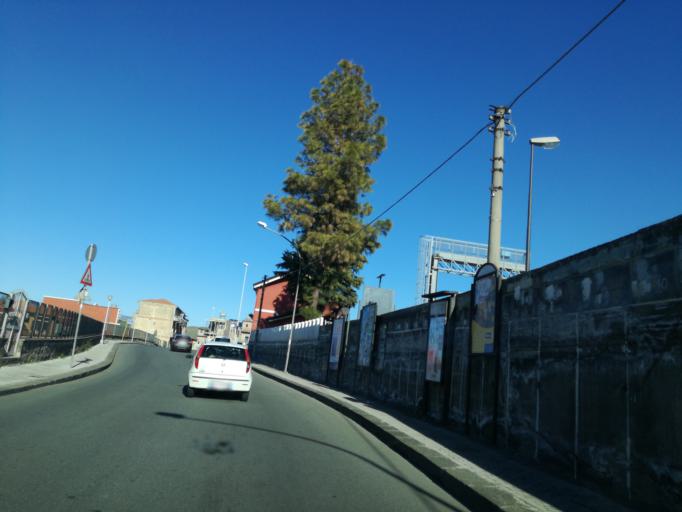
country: IT
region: Sicily
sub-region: Catania
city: Bronte
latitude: 37.7873
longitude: 14.8382
